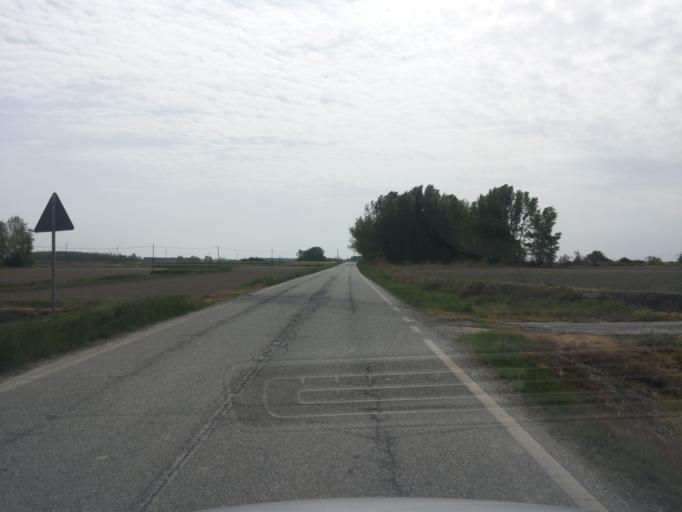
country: IT
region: Piedmont
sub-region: Provincia di Vercelli
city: Caresana
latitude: 45.2116
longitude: 8.5062
